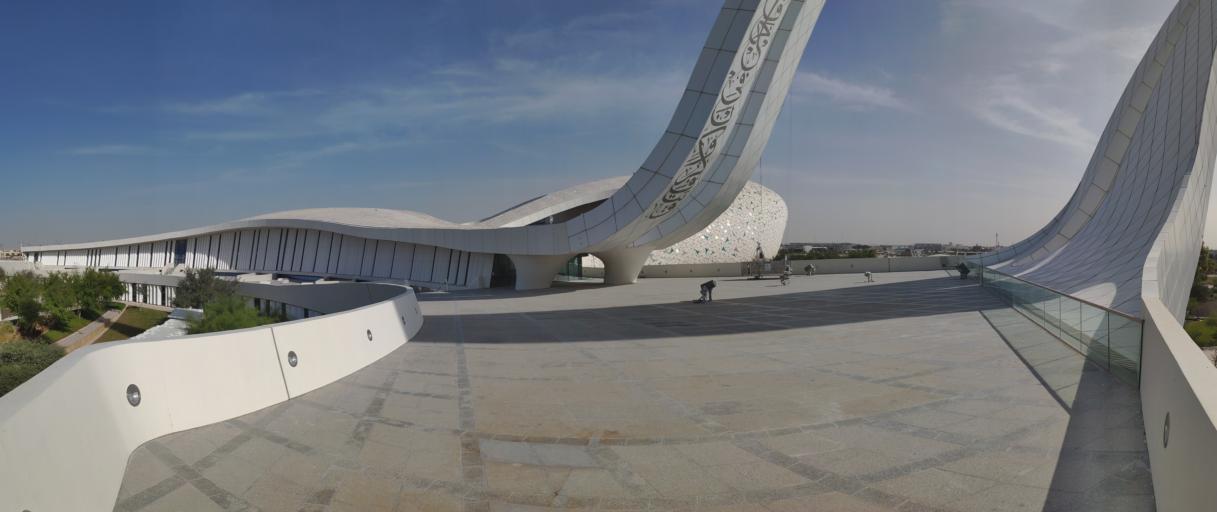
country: QA
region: Baladiyat ar Rayyan
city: Ar Rayyan
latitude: 25.3173
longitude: 51.4459
